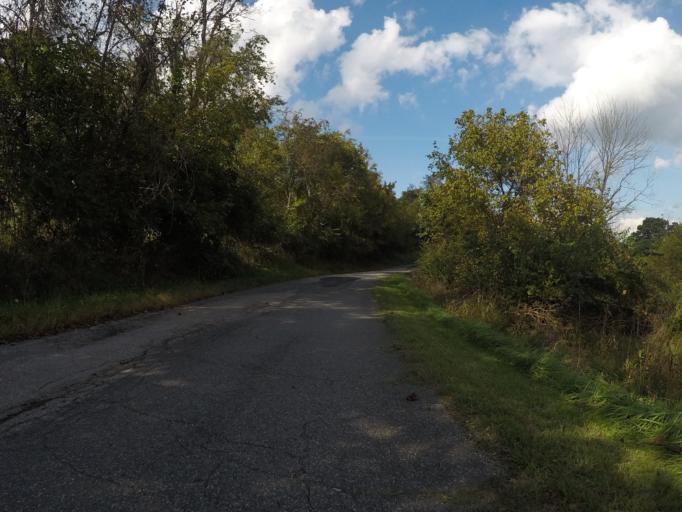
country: US
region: West Virginia
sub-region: Wayne County
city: Lavalette
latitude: 38.3654
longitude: -82.4736
